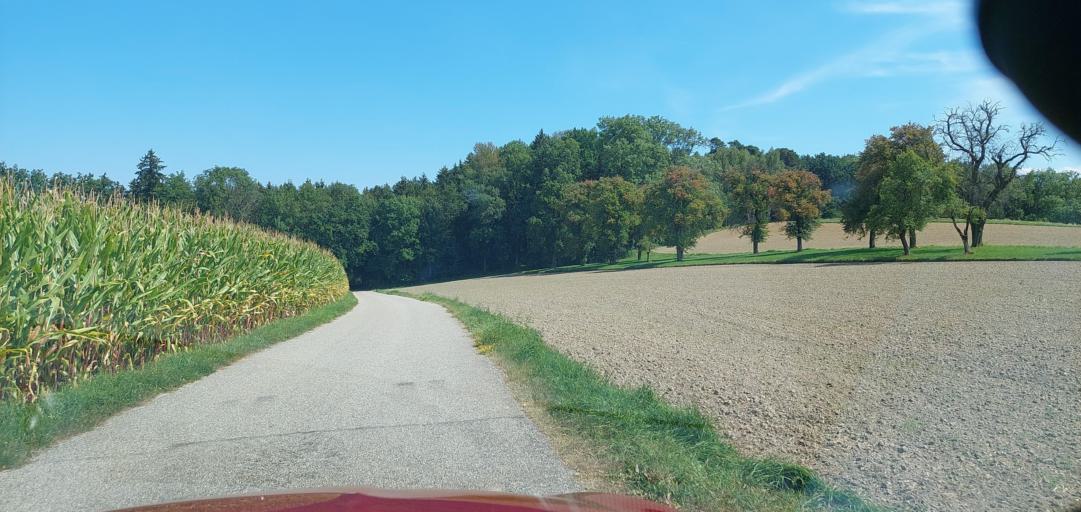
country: AT
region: Upper Austria
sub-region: Wels-Land
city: Pennewang
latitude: 48.1392
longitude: 13.8496
